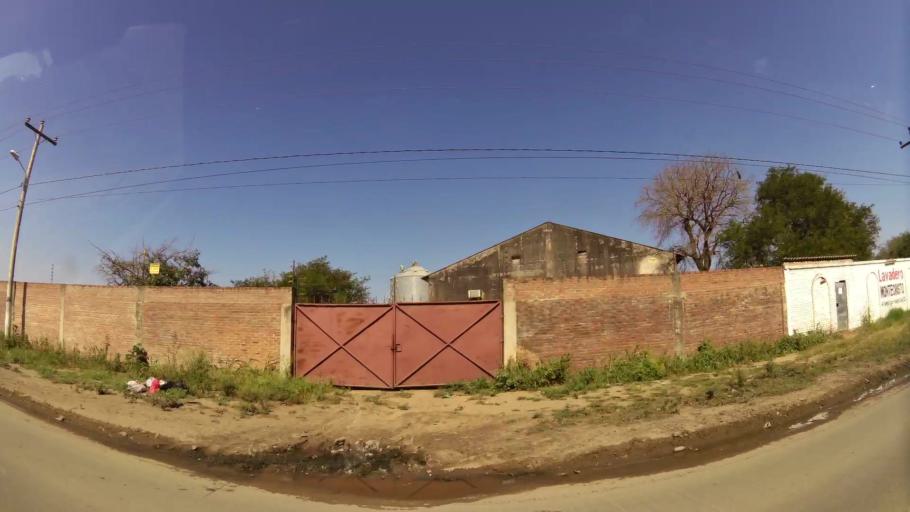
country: BO
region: Santa Cruz
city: Santa Cruz de la Sierra
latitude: -17.7660
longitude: -63.1136
